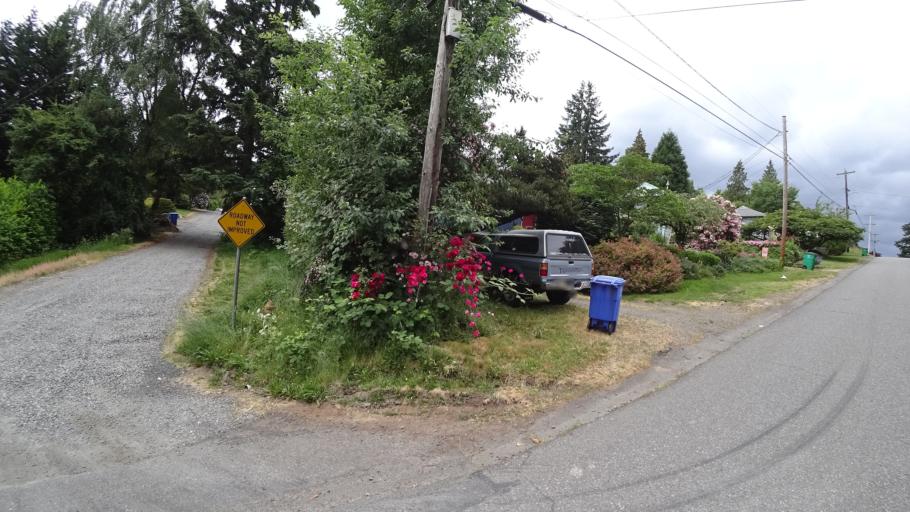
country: US
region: Oregon
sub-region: Clackamas County
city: Lake Oswego
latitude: 45.4598
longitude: -122.6952
